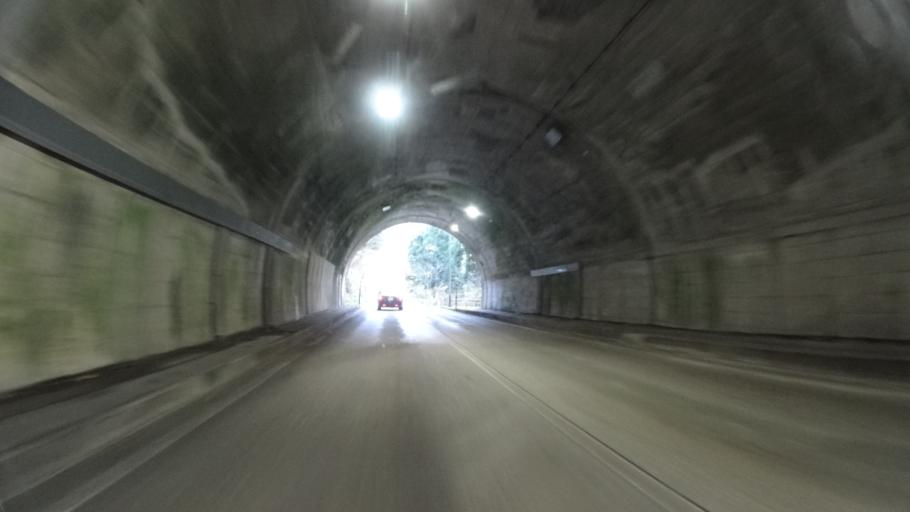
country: JP
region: Ishikawa
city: Tsurugi-asahimachi
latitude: 36.3732
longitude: 136.5738
